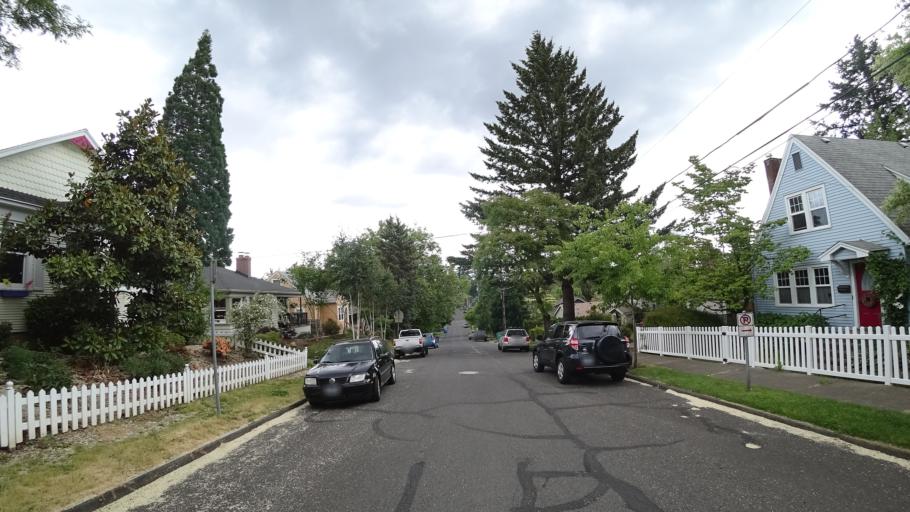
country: US
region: Oregon
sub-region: Clackamas County
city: Lake Oswego
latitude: 45.4642
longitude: -122.6951
